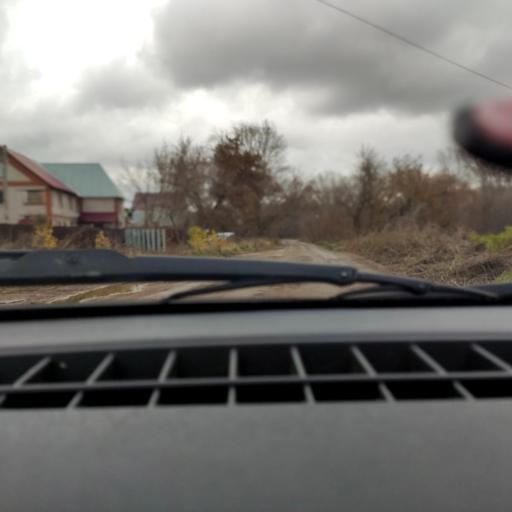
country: RU
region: Bashkortostan
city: Ufa
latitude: 54.7995
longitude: 56.1613
